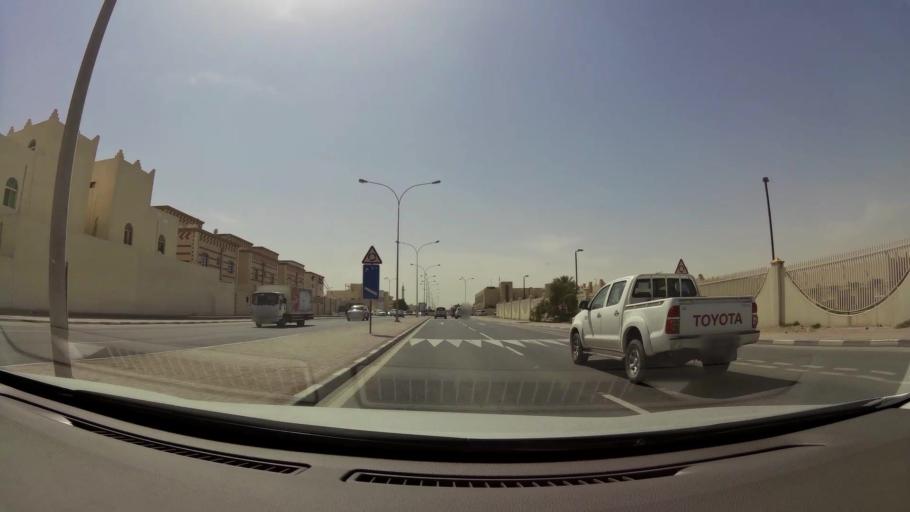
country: QA
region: Baladiyat ar Rayyan
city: Ar Rayyan
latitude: 25.2687
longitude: 51.4278
